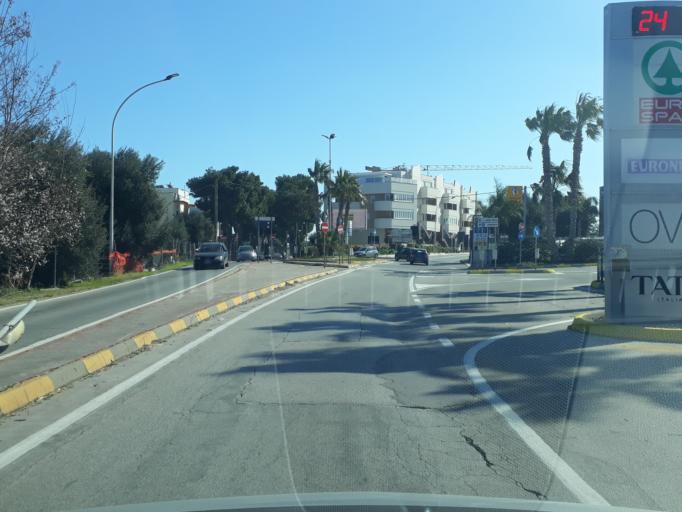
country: IT
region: Apulia
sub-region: Provincia di Bari
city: Monopoli
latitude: 40.9624
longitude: 17.2800
